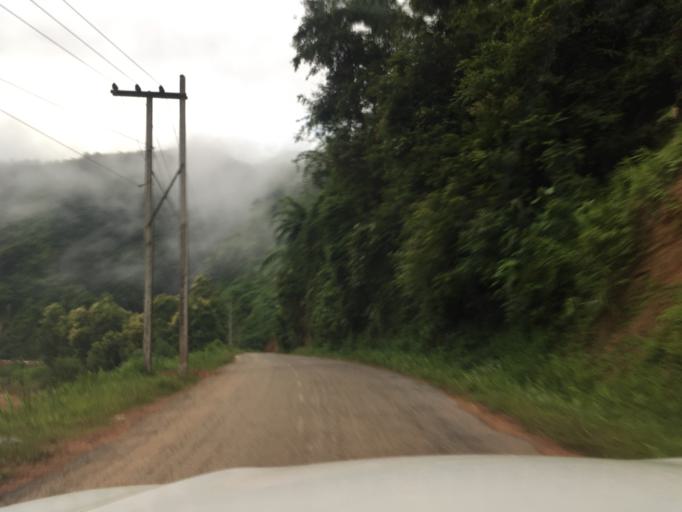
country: LA
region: Phongsali
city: Khoa
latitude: 21.0741
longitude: 102.3766
